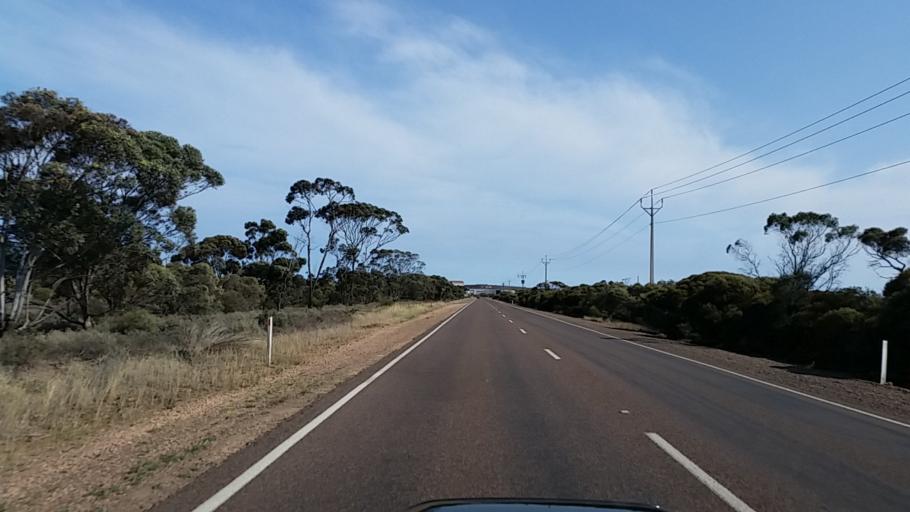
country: AU
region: South Australia
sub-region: Whyalla
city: Whyalla
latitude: -32.9928
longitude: 137.5793
